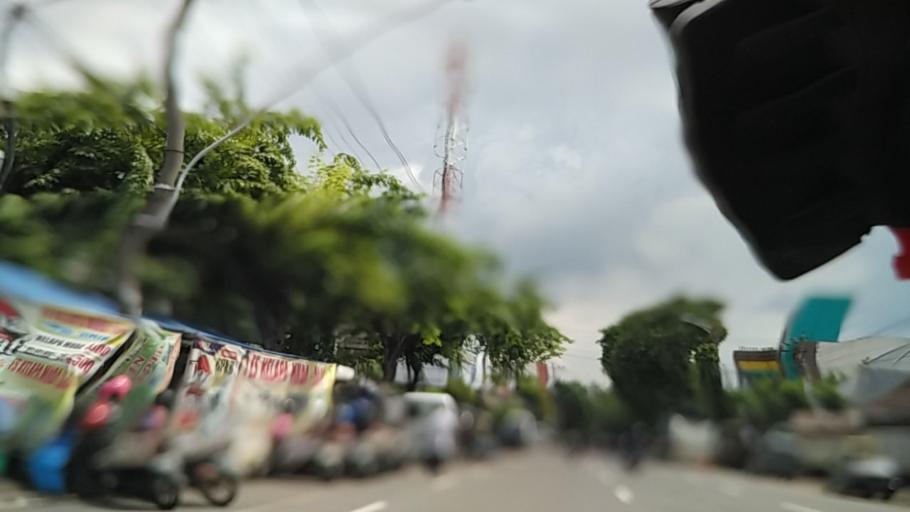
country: ID
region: Central Java
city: Semarang
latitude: -6.9771
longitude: 110.4352
